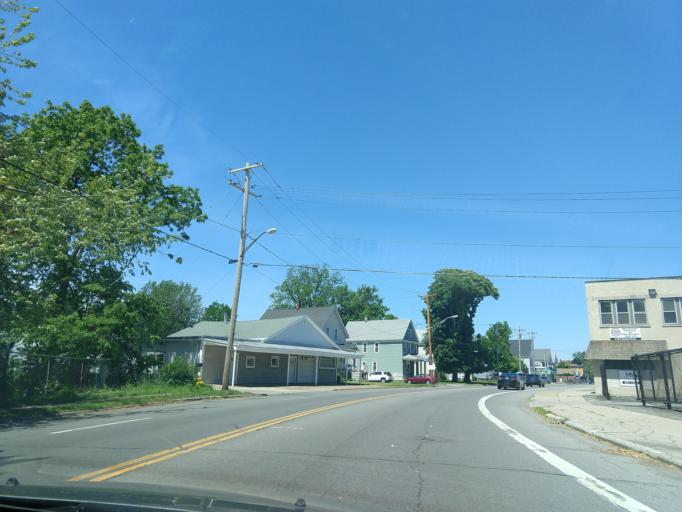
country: US
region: New York
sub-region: Erie County
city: West Seneca
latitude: 42.8463
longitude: -78.7989
